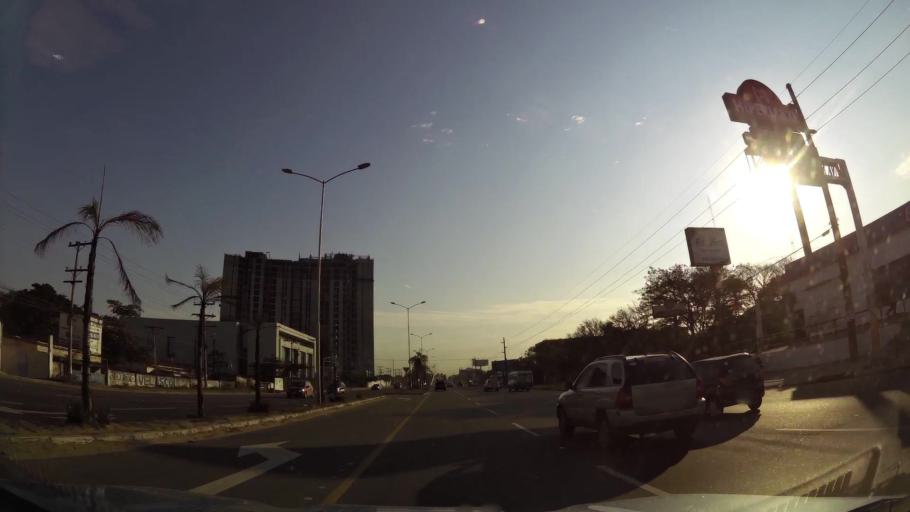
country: BO
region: Santa Cruz
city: Santa Cruz de la Sierra
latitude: -17.7283
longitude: -63.1667
